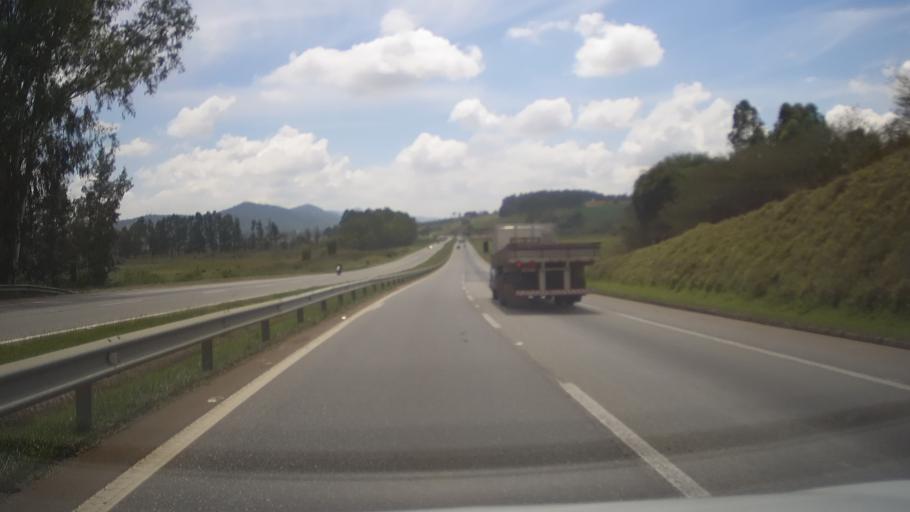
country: BR
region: Minas Gerais
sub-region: Santa Rita Do Sapucai
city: Santa Rita do Sapucai
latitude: -22.0986
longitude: -45.7193
